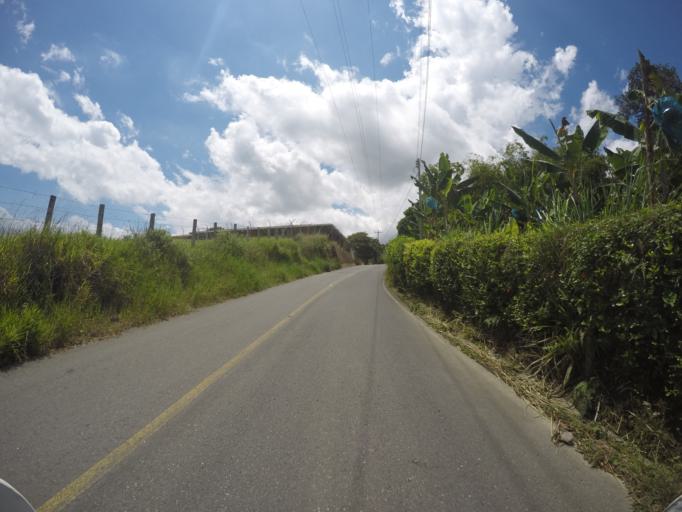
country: CO
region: Quindio
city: Quimbaya
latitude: 4.6286
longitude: -75.7232
